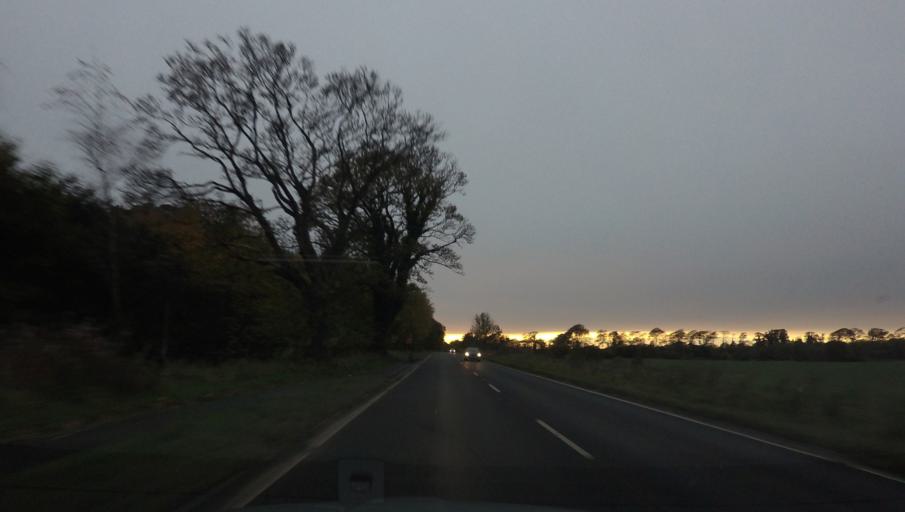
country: GB
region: Scotland
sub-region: Fife
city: Crossford
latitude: 56.0450
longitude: -3.4956
